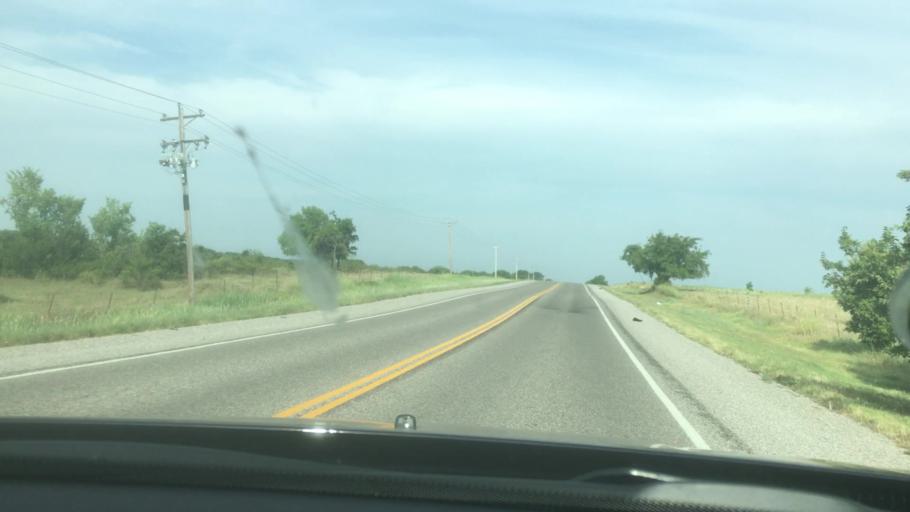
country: US
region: Oklahoma
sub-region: Garvin County
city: Stratford
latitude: 34.7966
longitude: -97.0919
